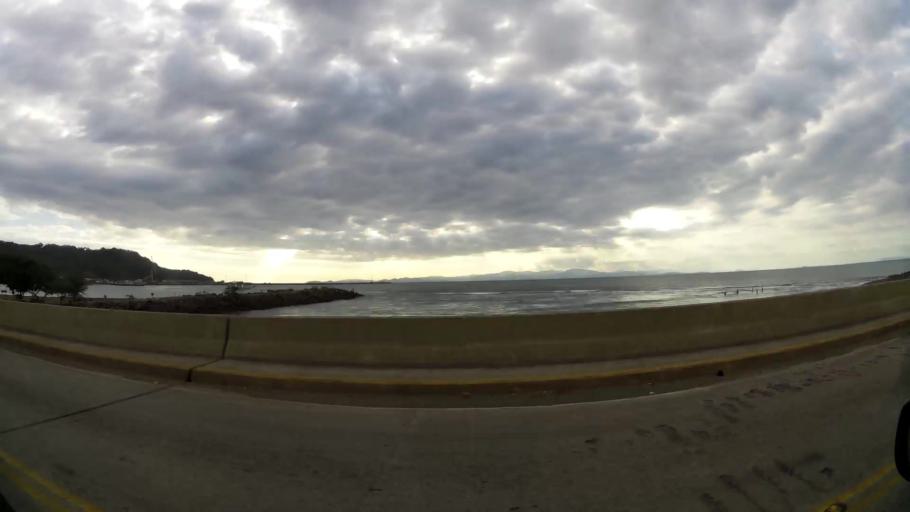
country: CR
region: Puntarenas
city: Esparza
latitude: 9.9225
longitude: -84.7134
